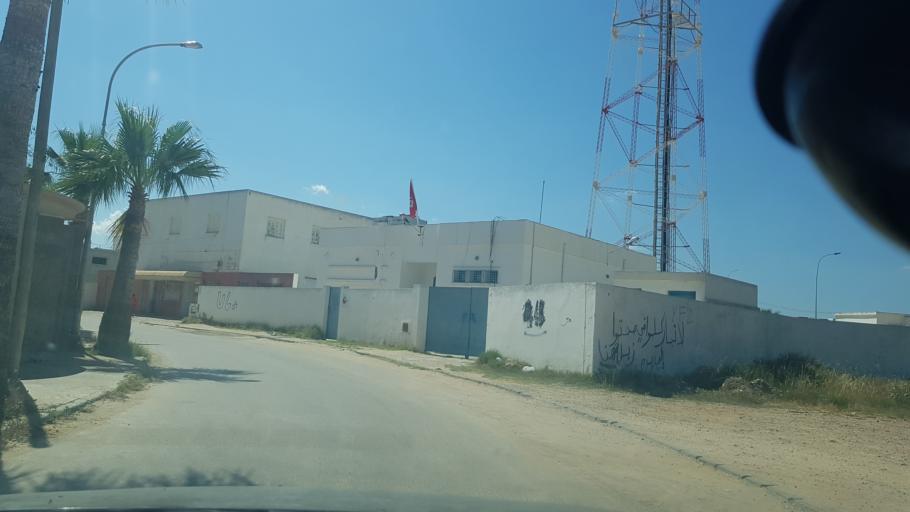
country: TN
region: Safaqis
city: Al Qarmadah
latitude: 34.8268
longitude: 10.7576
